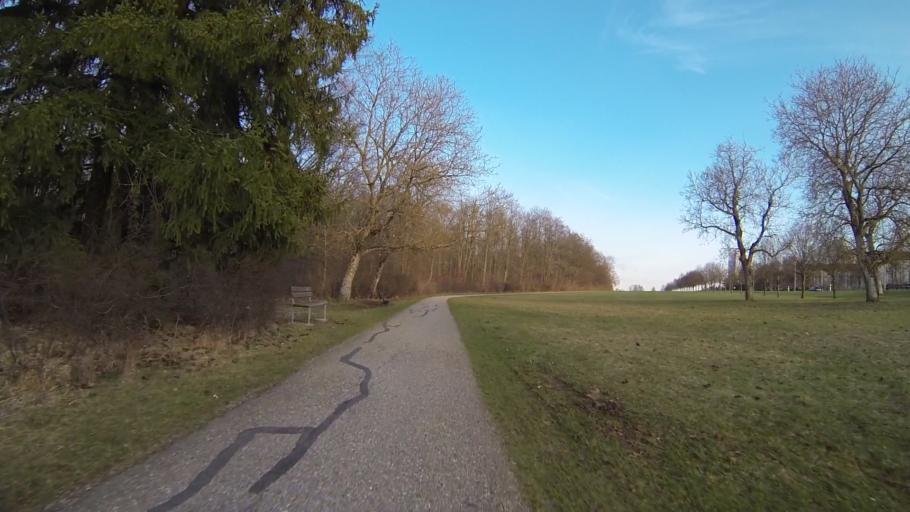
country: DE
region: Baden-Wuerttemberg
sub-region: Regierungsbezirk Stuttgart
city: Heidenheim an der Brenz
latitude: 48.6945
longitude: 10.1360
